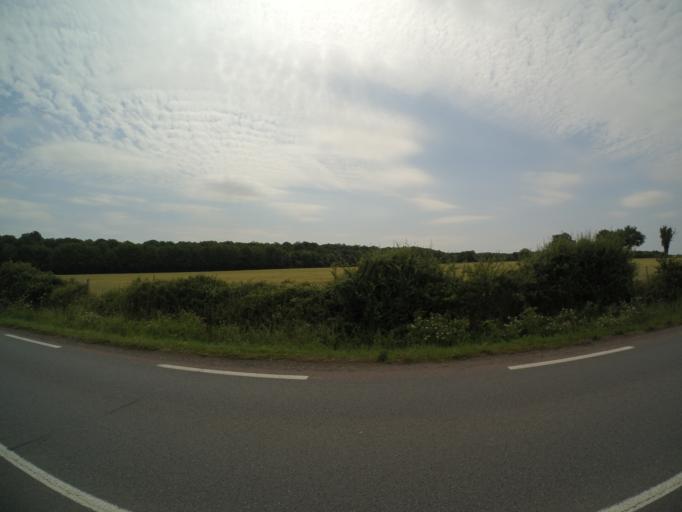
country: FR
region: Pays de la Loire
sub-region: Departement de la Vendee
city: Vendrennes
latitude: 46.8357
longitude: -1.0967
